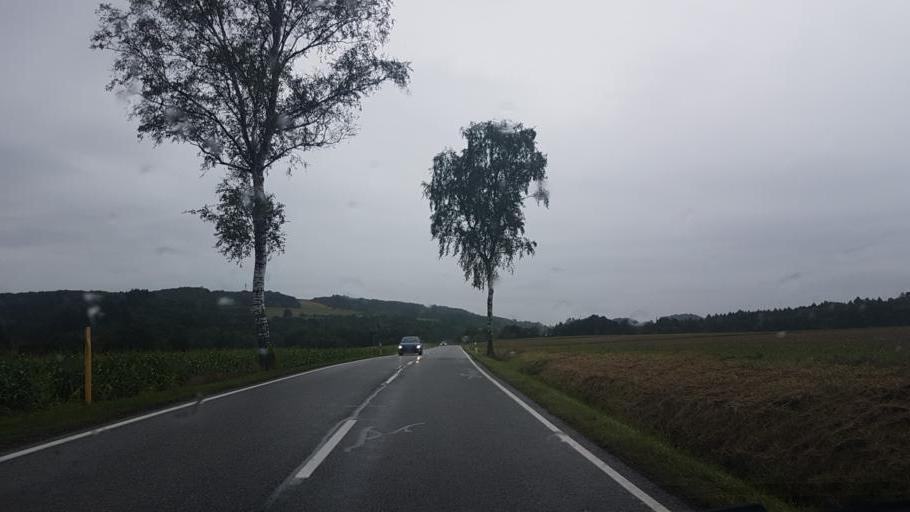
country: DE
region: Saarland
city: Wadern
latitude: 49.4973
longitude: 6.8514
